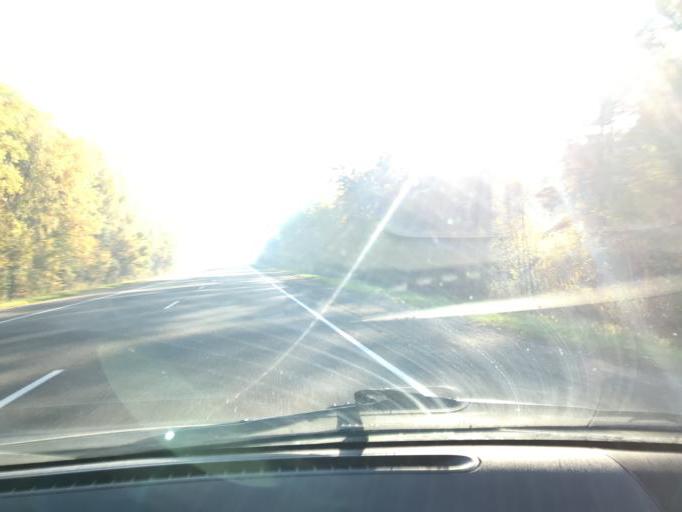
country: BY
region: Brest
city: Horad Luninyets
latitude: 52.3097
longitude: 26.6749
